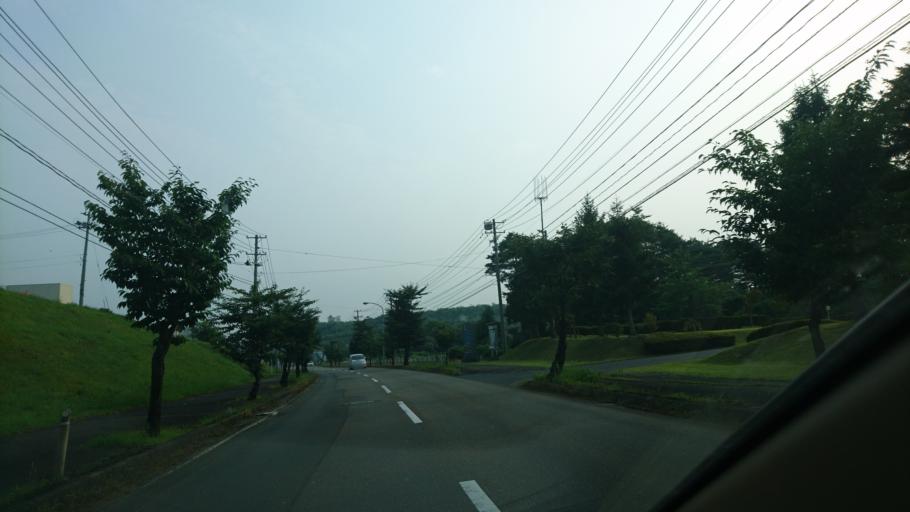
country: JP
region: Iwate
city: Mizusawa
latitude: 39.2099
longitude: 141.1797
